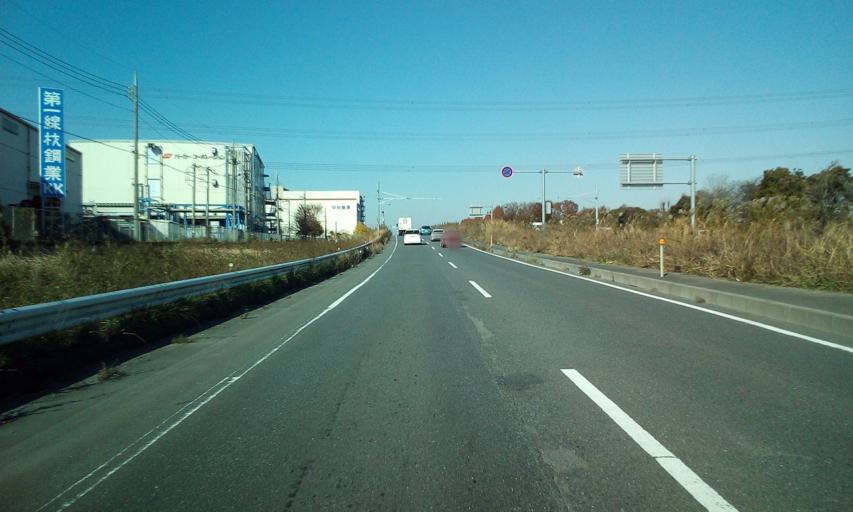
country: JP
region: Ibaraki
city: Sakai
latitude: 36.0786
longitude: 139.7706
